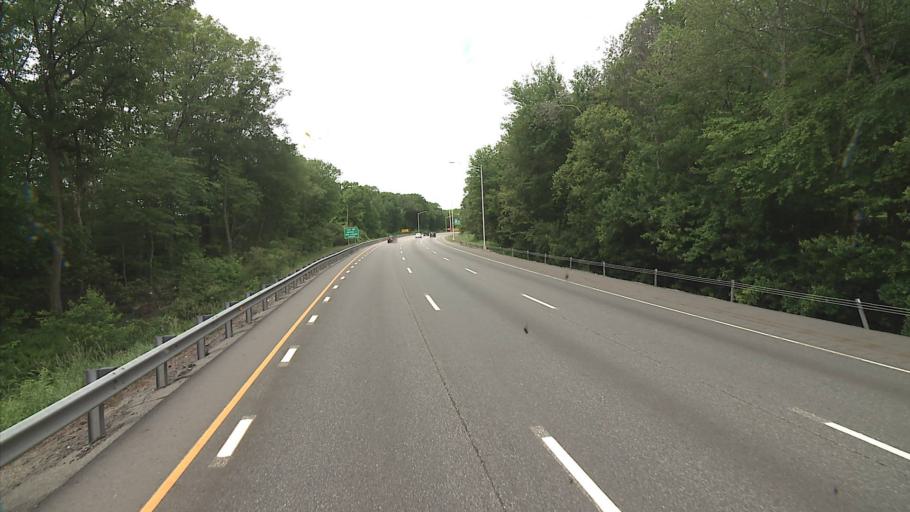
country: US
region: Connecticut
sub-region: New London County
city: Long Hill
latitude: 41.3596
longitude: -72.0468
